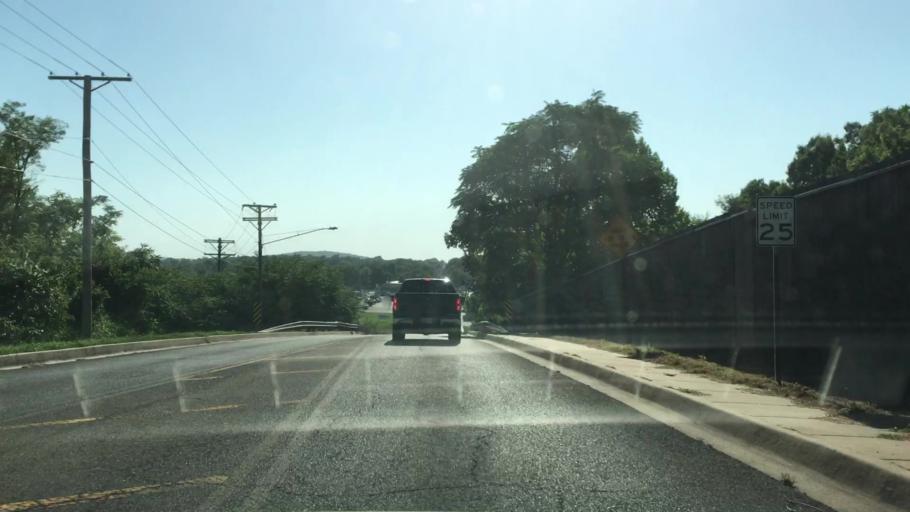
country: US
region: Oklahoma
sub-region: Cherokee County
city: Tahlequah
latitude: 35.9008
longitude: -94.9698
